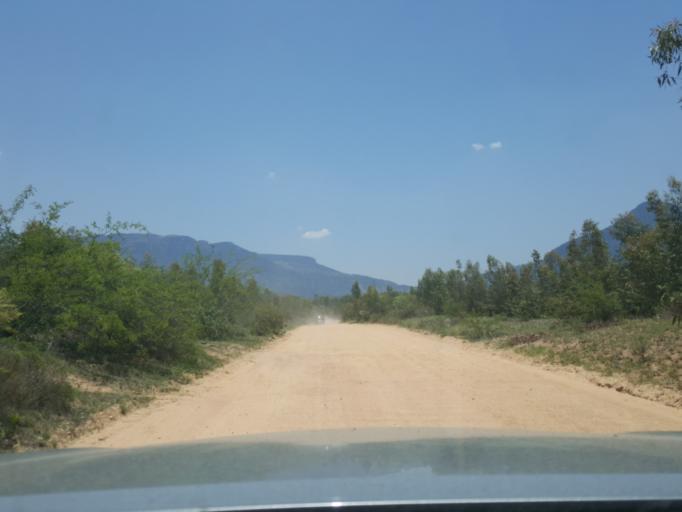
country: ZA
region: Limpopo
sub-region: Mopani District Municipality
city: Hoedspruit
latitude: -24.5873
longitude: 30.9673
